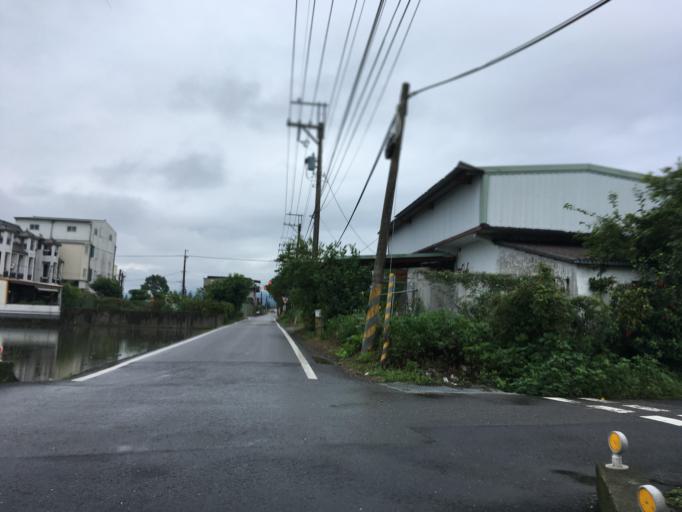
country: TW
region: Taiwan
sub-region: Yilan
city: Yilan
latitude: 24.6671
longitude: 121.7429
